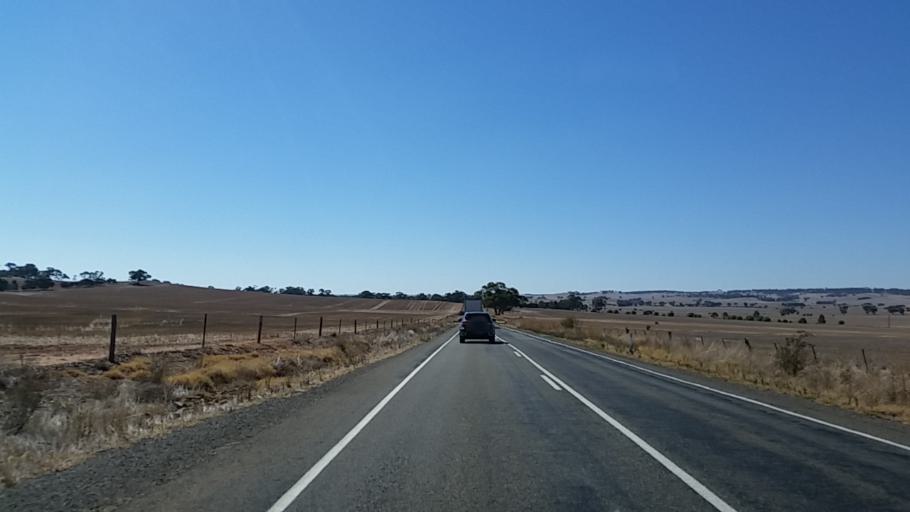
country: AU
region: South Australia
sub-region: Clare and Gilbert Valleys
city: Clare
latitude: -34.0216
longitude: 138.8069
